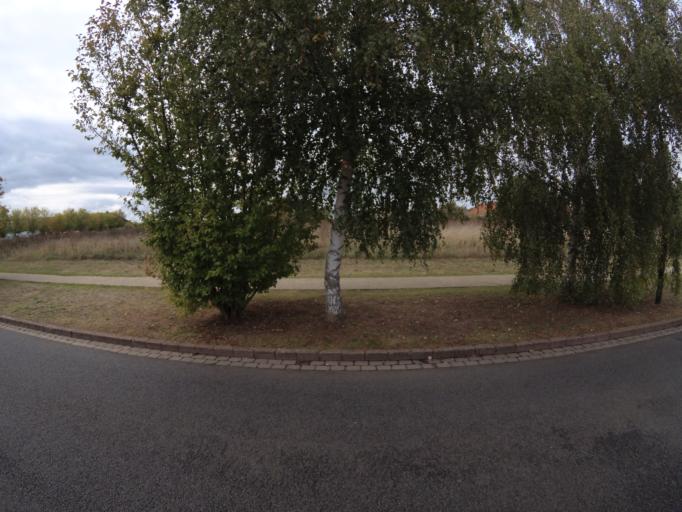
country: FR
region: Ile-de-France
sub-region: Departement de Seine-et-Marne
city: Chessy
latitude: 48.8734
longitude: 2.7668
